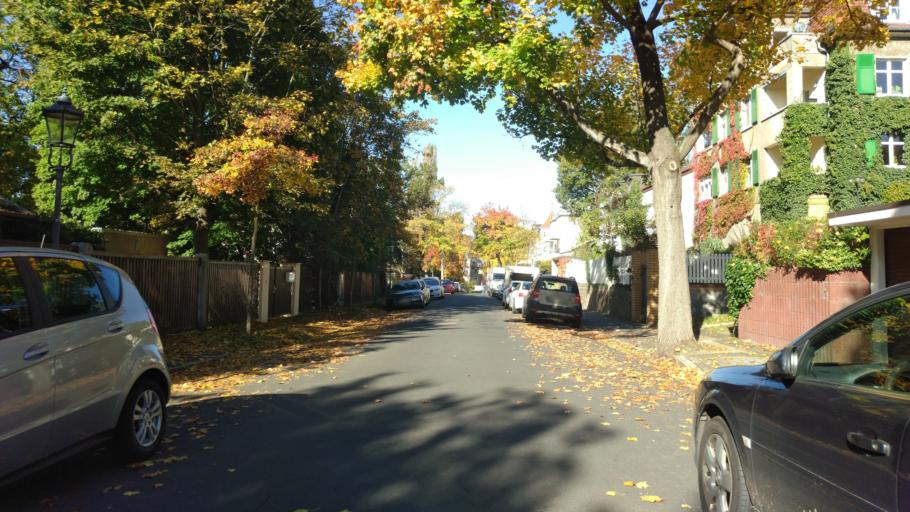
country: DE
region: Saxony
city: Albertstadt
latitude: 51.0931
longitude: 13.7325
